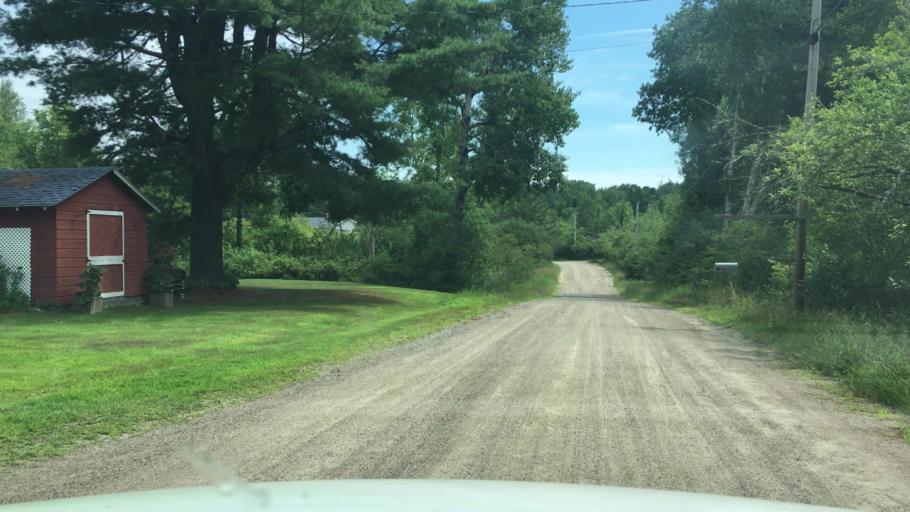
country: CA
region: New Brunswick
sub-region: Charlotte County
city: Saint Andrews
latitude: 45.0363
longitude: -67.1150
